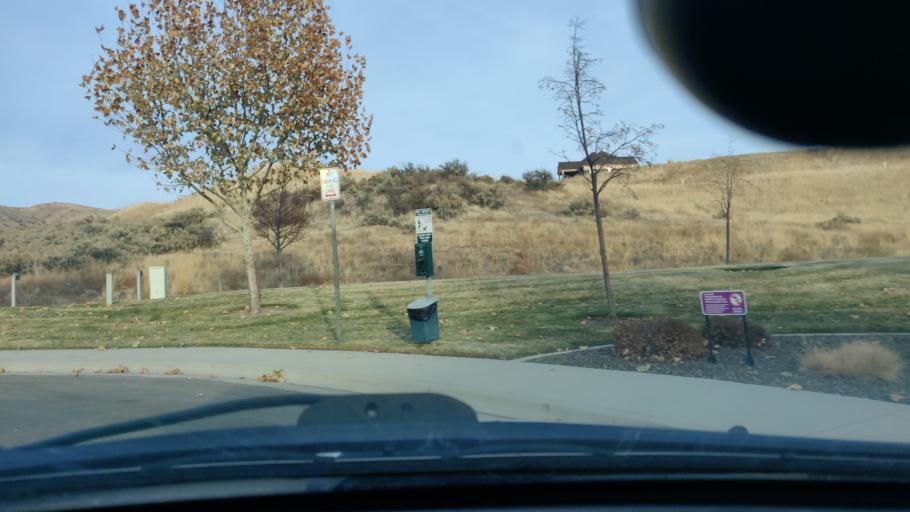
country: US
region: Idaho
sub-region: Ada County
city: Eagle
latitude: 43.7761
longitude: -116.2614
